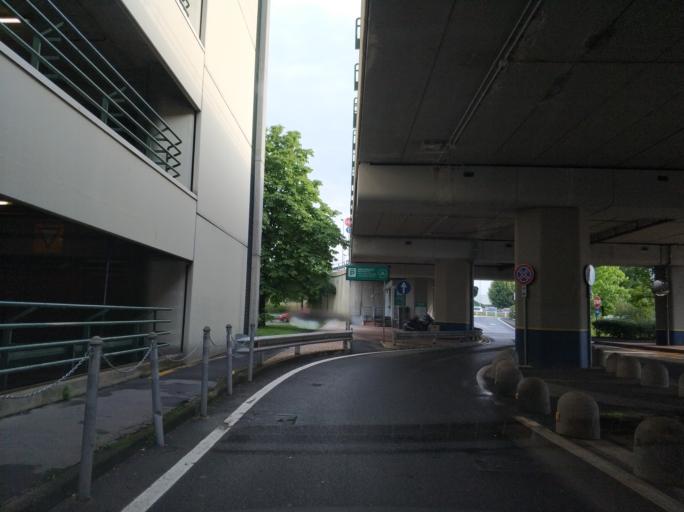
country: IT
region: Piedmont
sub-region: Provincia di Torino
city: Caselle Torinese
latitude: 45.1926
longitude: 7.6428
